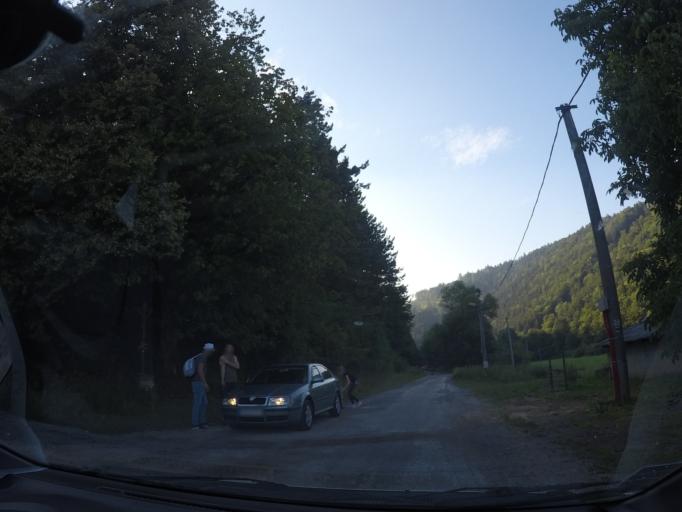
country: SK
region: Nitriansky
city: Bojnice
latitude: 48.9050
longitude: 18.6043
